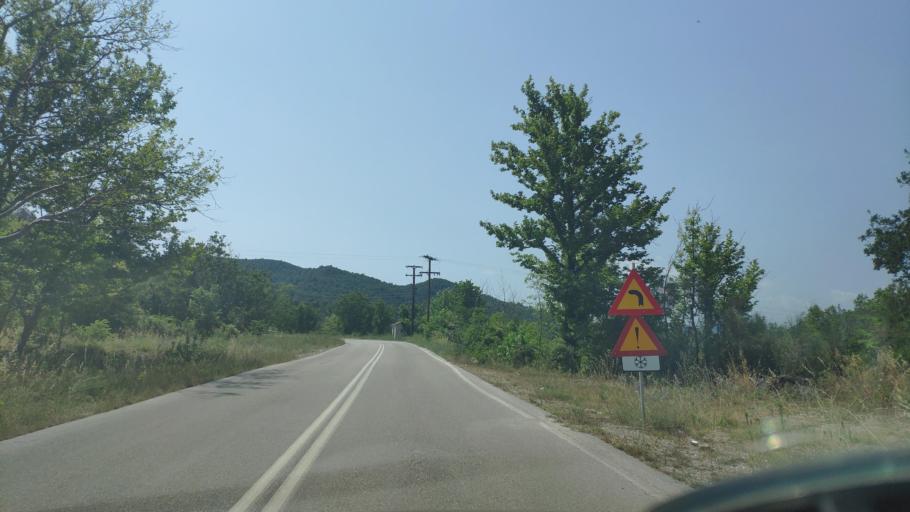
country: GR
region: Epirus
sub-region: Nomos Artas
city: Ano Kalentini
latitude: 39.2270
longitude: 21.1498
